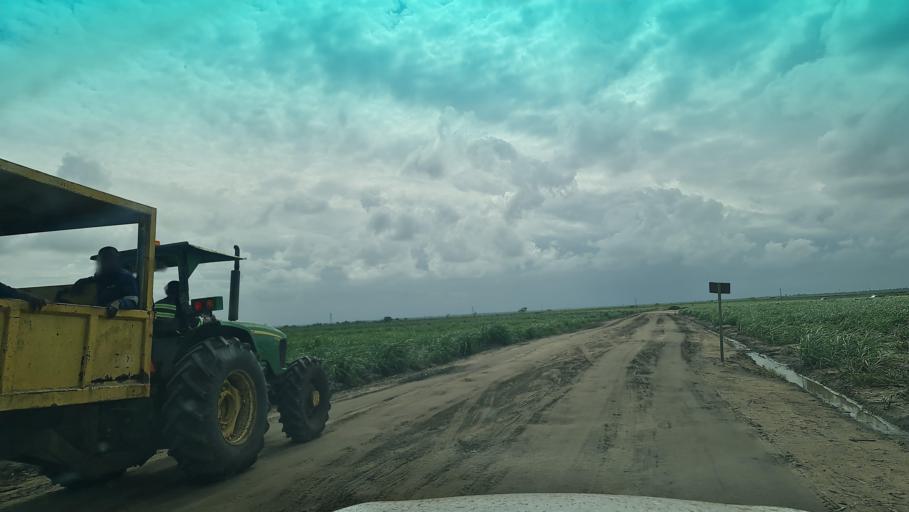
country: MZ
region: Maputo
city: Manhica
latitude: -25.4774
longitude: 32.8164
